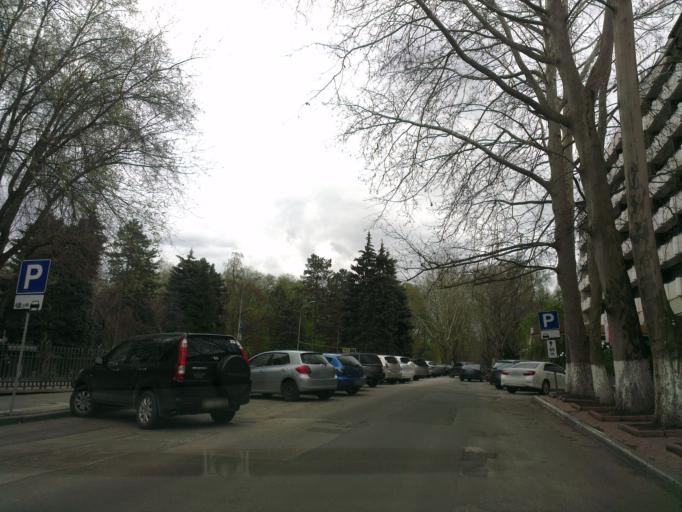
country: MD
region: Chisinau
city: Chisinau
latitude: 47.0254
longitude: 28.8252
